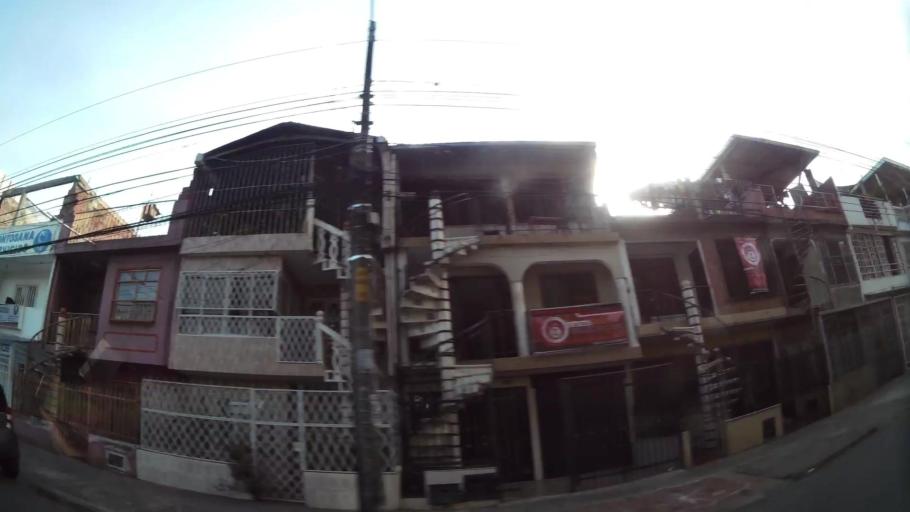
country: CO
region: Valle del Cauca
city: Cali
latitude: 3.3994
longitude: -76.5087
